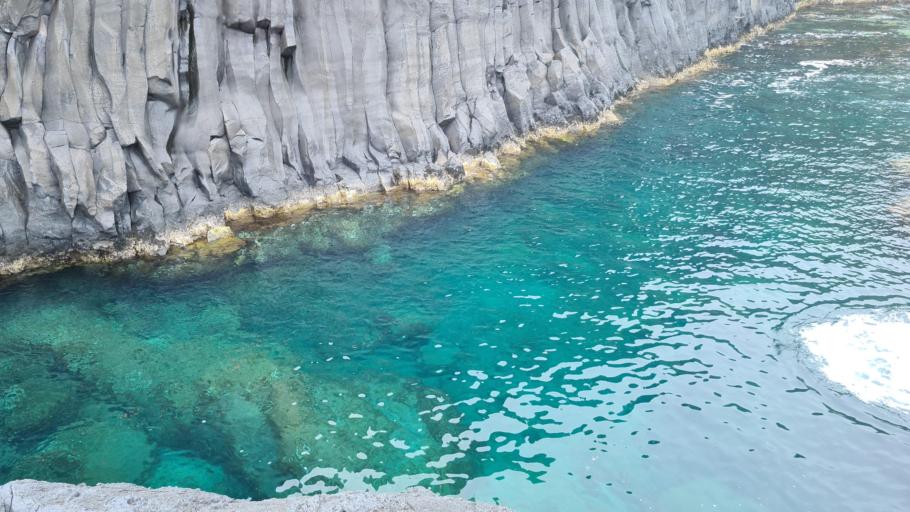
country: PT
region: Azores
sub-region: Sao Roque do Pico
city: Sao Roque do Pico
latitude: 38.6794
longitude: -28.0534
